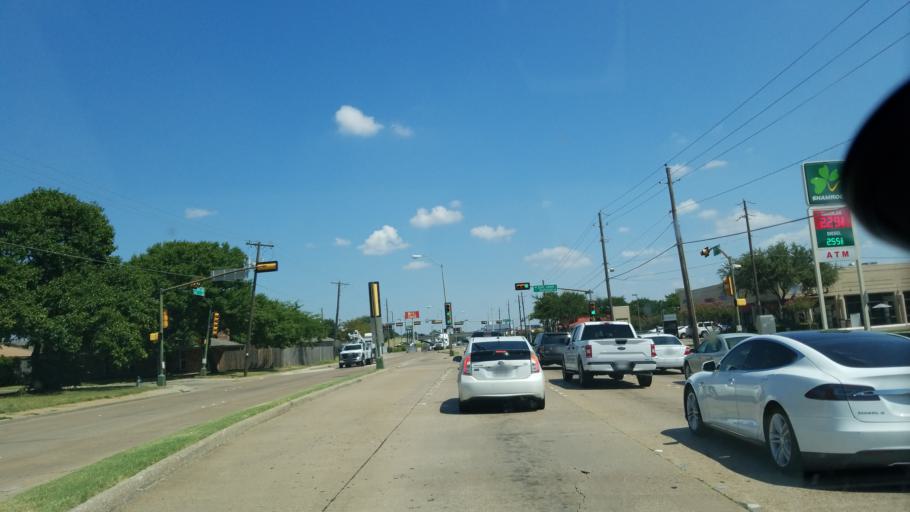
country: US
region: Texas
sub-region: Dallas County
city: Duncanville
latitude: 32.6562
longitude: -96.8913
